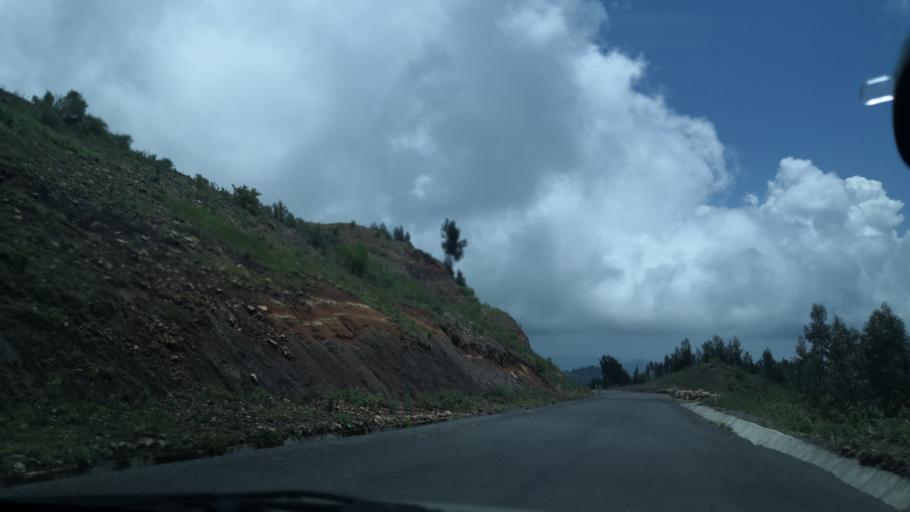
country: ET
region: Amhara
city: Kemise
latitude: 10.3633
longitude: 39.8288
